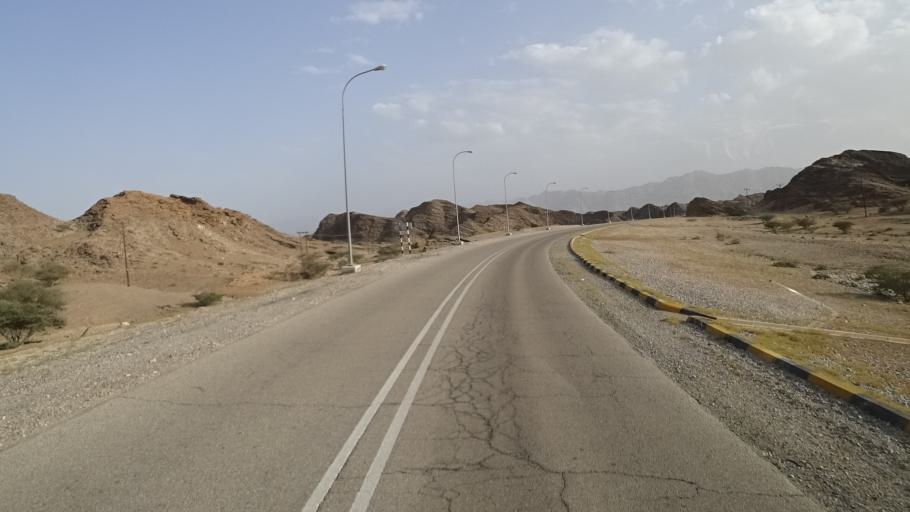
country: OM
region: Muhafazat Masqat
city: Bawshar
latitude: 23.3684
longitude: 58.5257
